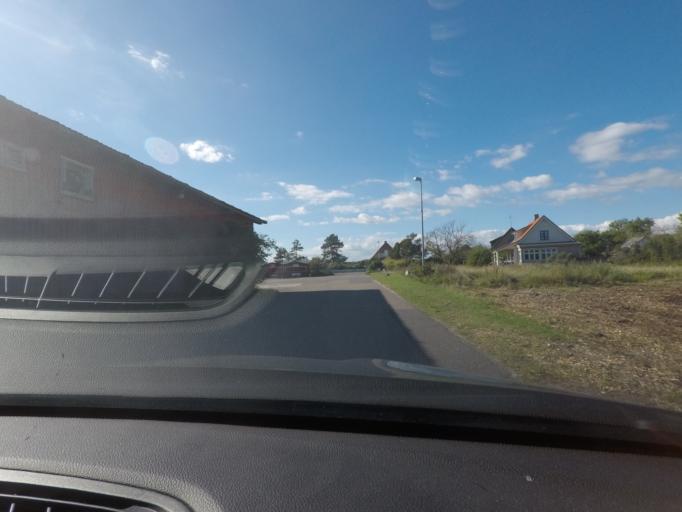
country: DK
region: Zealand
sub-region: Lolland Kommune
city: Maribo
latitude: 54.9729
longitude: 11.5147
